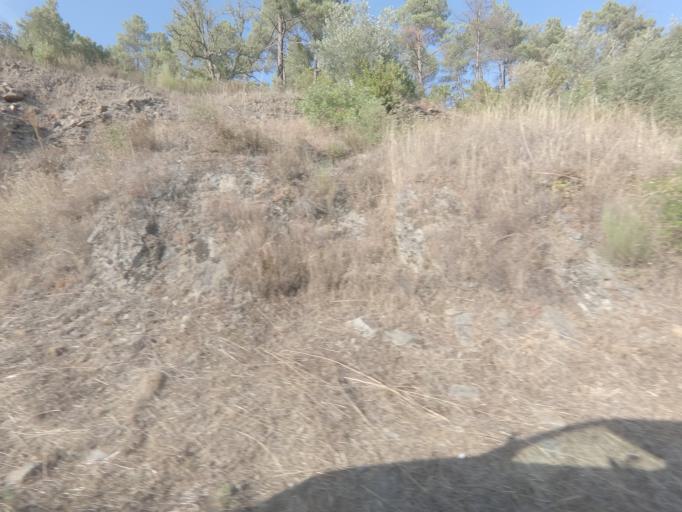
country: PT
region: Vila Real
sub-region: Sabrosa
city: Sabrosa
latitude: 41.2414
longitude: -7.5230
